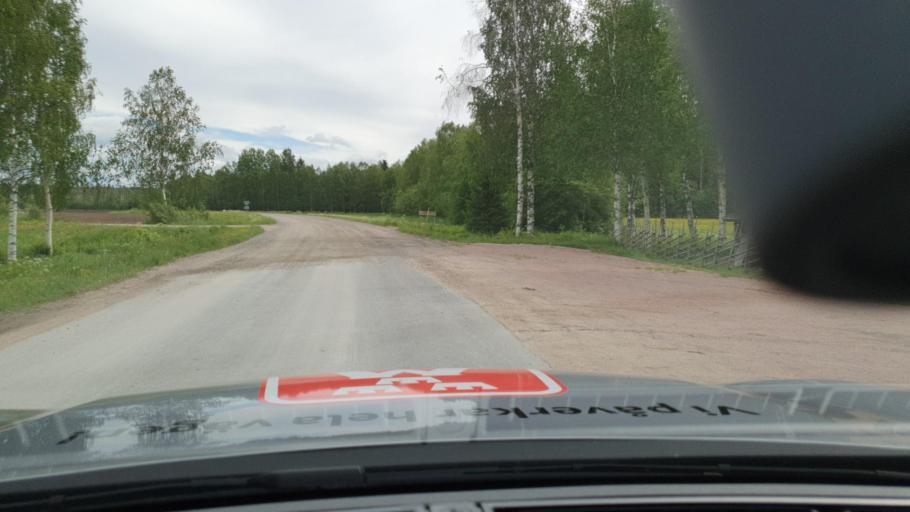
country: SE
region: Norrbotten
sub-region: Kalix Kommun
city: Kalix
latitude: 65.9205
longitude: 23.4618
